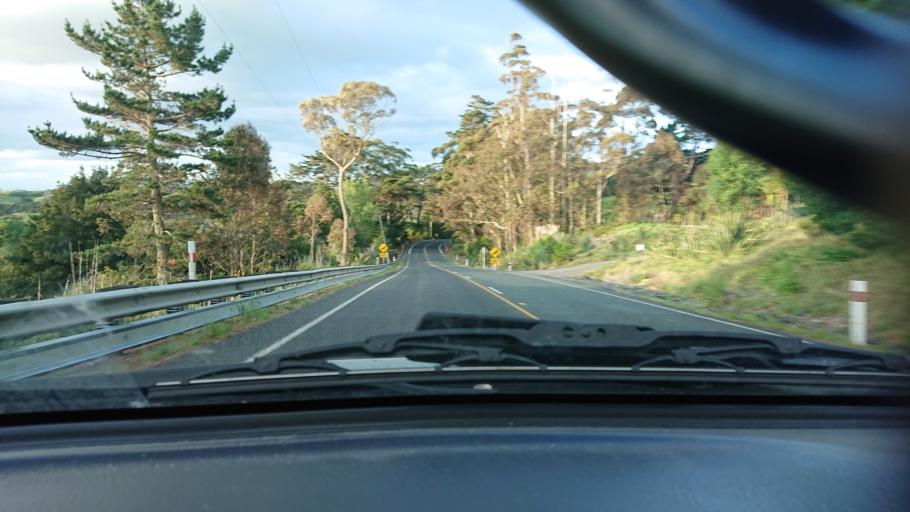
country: NZ
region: Auckland
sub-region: Auckland
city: Parakai
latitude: -36.5390
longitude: 174.4558
